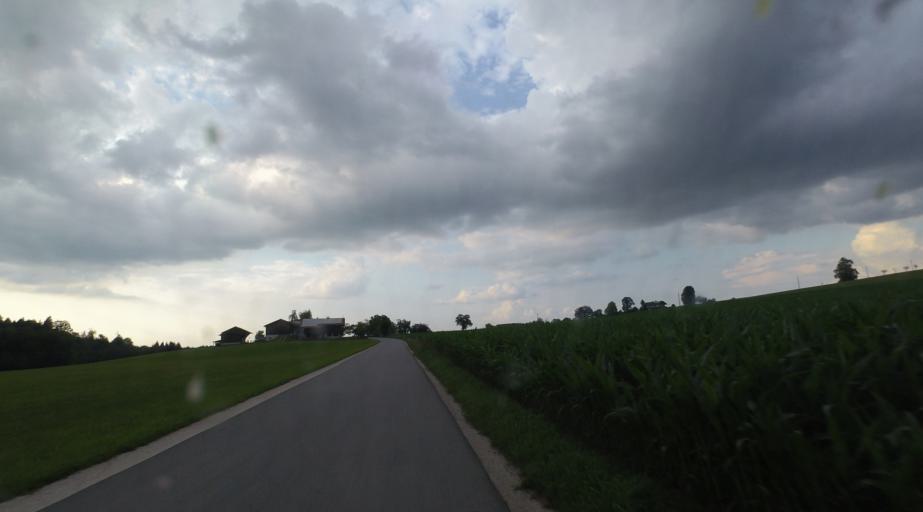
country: DE
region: Bavaria
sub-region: Upper Bavaria
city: Grabenstatt
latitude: 47.8322
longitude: 12.5456
